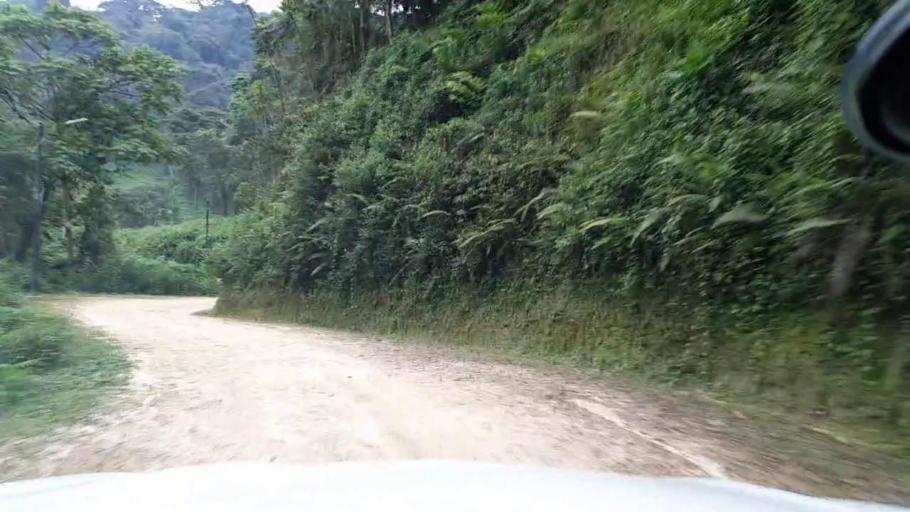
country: RW
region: Western Province
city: Cyangugu
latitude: -2.5671
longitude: 29.2315
